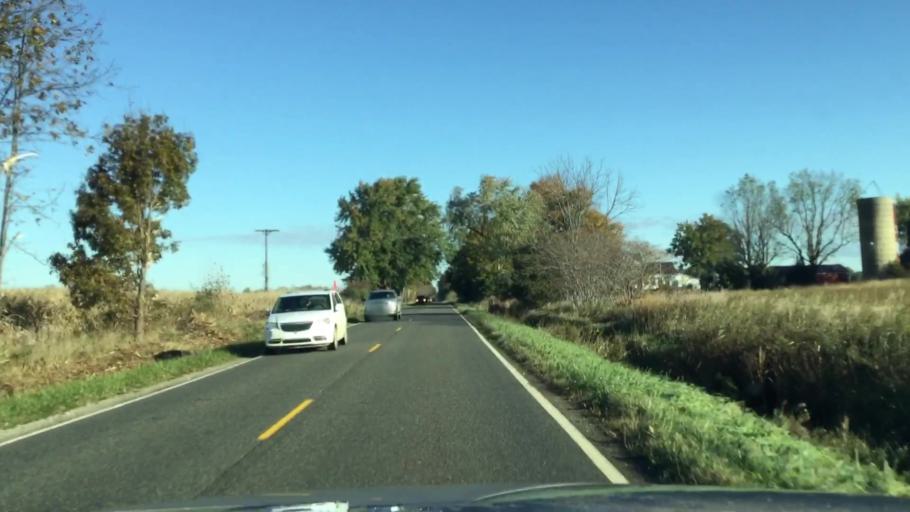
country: US
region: Michigan
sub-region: Genesee County
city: Argentine
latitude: 42.7988
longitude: -83.9430
